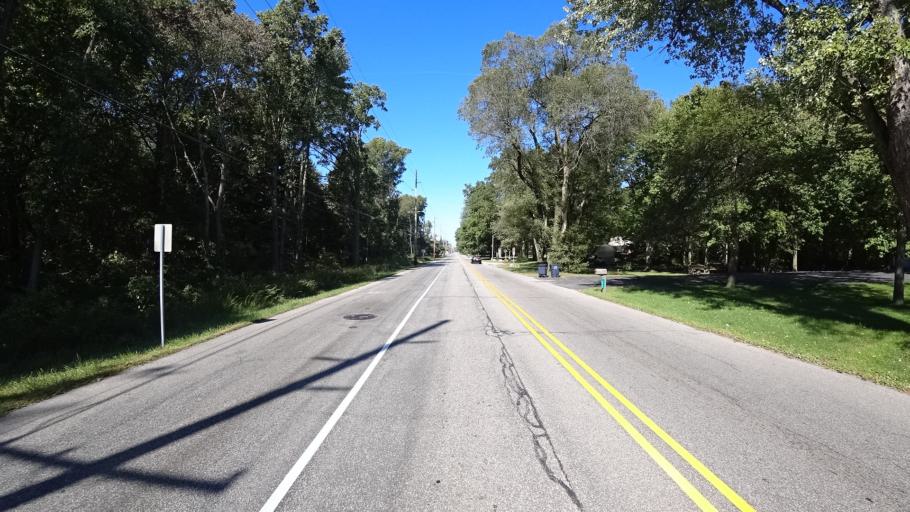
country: US
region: Indiana
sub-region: LaPorte County
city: Michigan City
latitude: 41.6838
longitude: -86.9038
